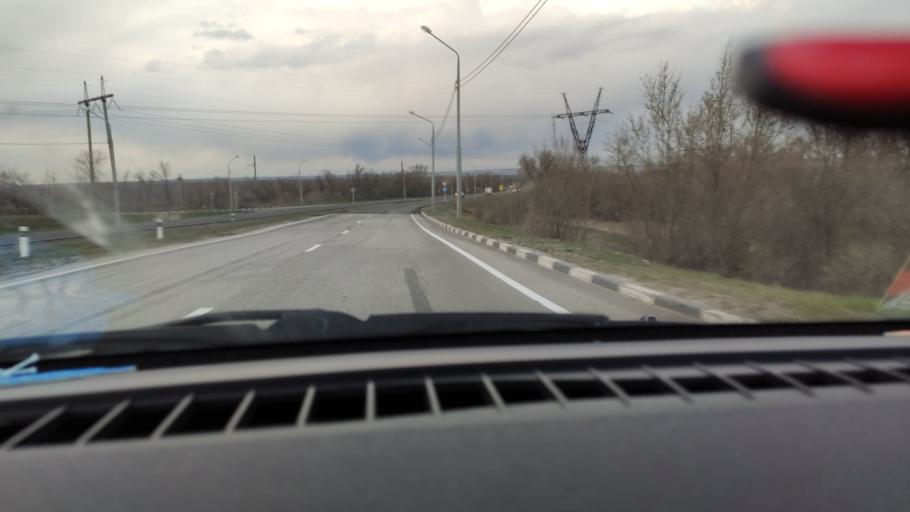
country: RU
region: Saratov
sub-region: Saratovskiy Rayon
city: Saratov
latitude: 51.6765
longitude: 46.0010
